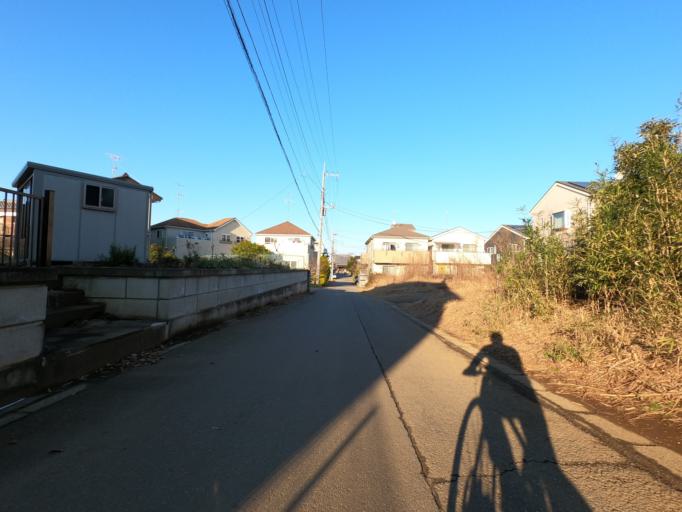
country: JP
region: Ibaraki
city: Moriya
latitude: 35.9397
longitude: 139.9987
